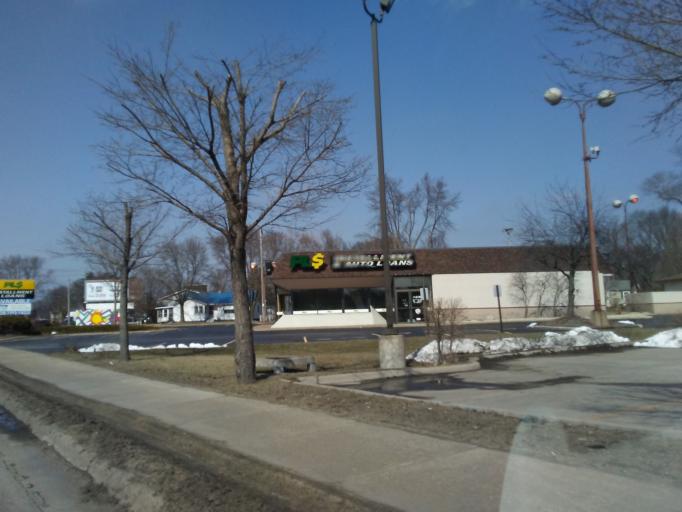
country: US
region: Wisconsin
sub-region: La Crosse County
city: La Crosse
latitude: 43.7742
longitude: -91.2188
